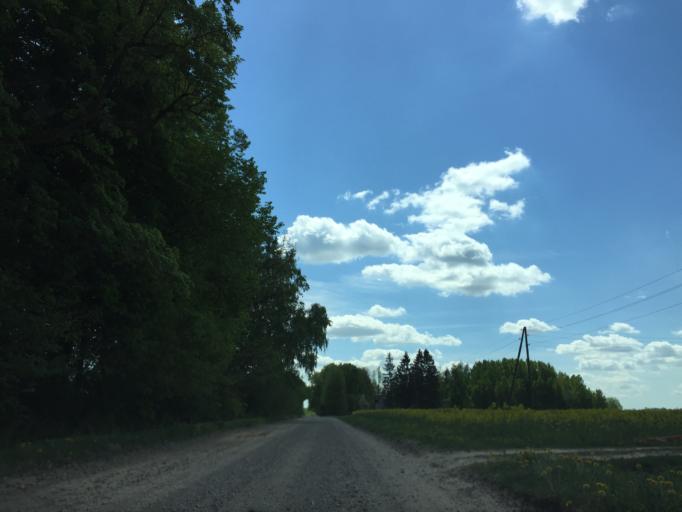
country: LV
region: Bauskas Rajons
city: Bauska
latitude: 56.4935
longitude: 24.1243
